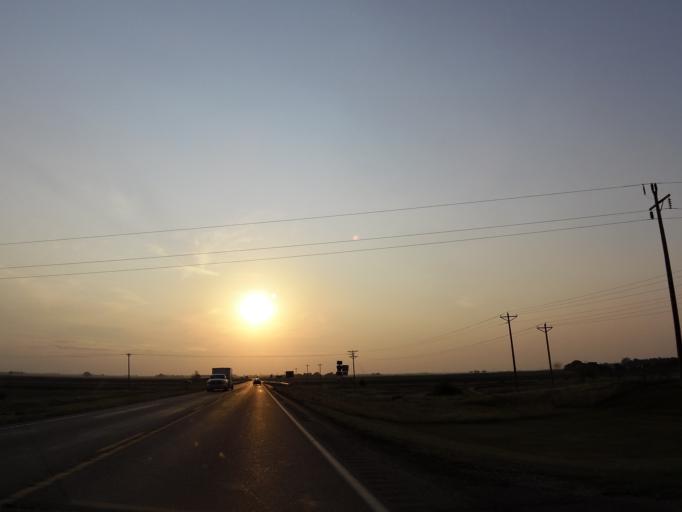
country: US
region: North Dakota
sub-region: Grand Forks County
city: Larimore
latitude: 47.7442
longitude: -97.6215
